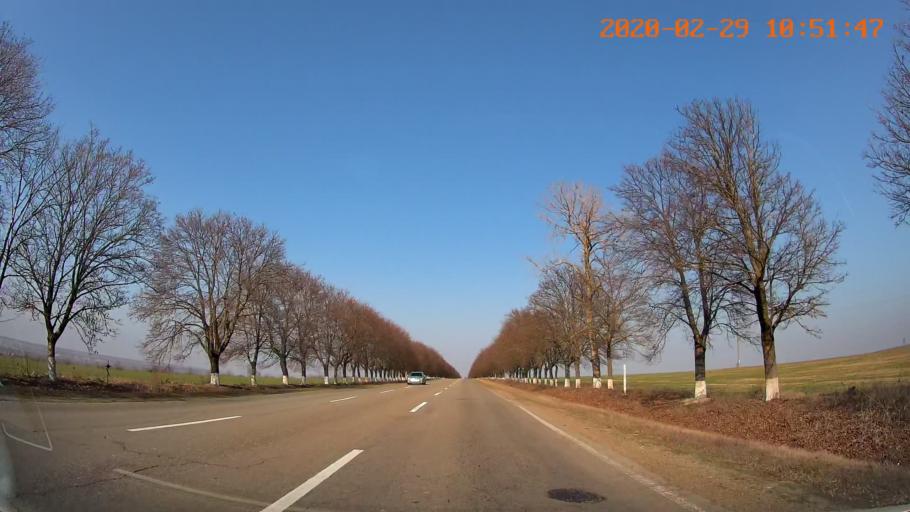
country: MD
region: Telenesti
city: Grigoriopol
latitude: 47.0970
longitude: 29.3596
